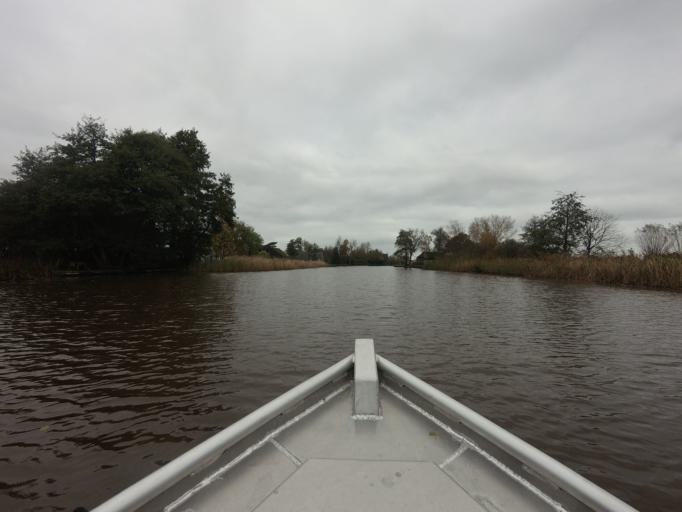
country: NL
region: Overijssel
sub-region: Gemeente Steenwijkerland
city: Blokzijl
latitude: 52.7522
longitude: 5.9949
